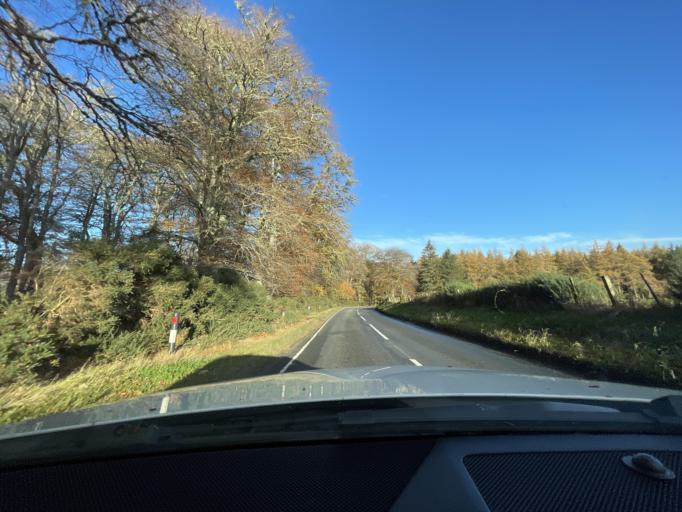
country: GB
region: Scotland
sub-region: Highland
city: Inverness
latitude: 57.4218
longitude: -4.2958
